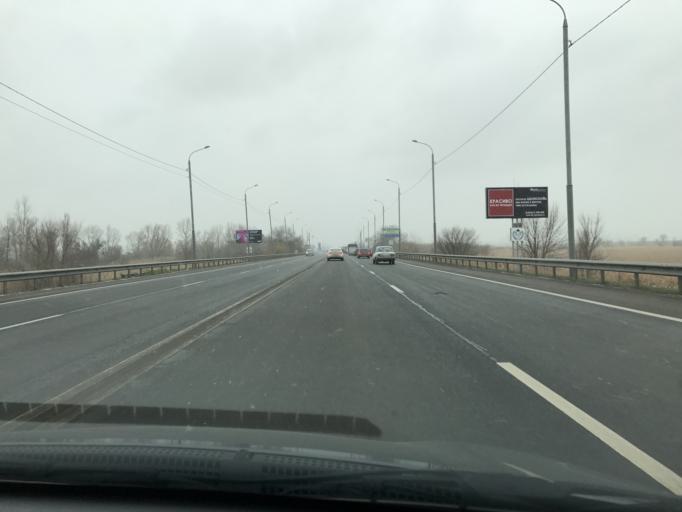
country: RU
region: Rostov
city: Rostov-na-Donu
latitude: 47.1873
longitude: 39.7360
